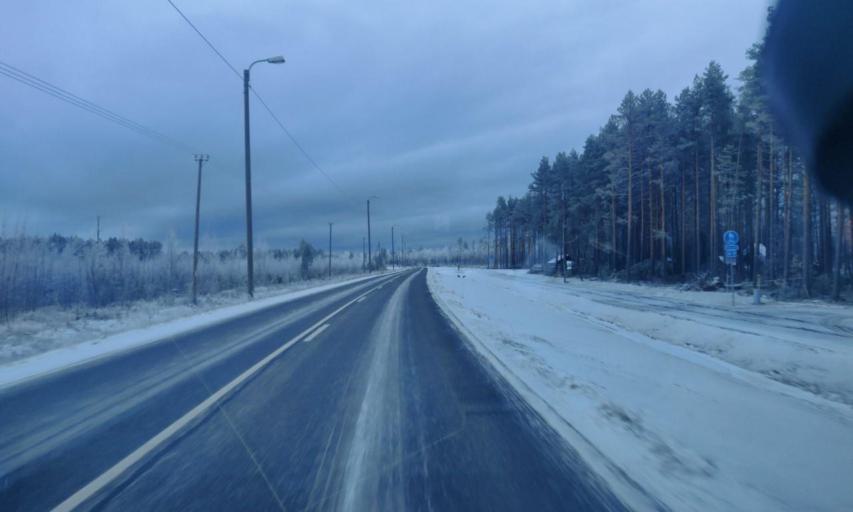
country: FI
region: Northern Ostrobothnia
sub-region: Oulu
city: Oulunsalo
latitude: 64.9892
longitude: 25.2579
